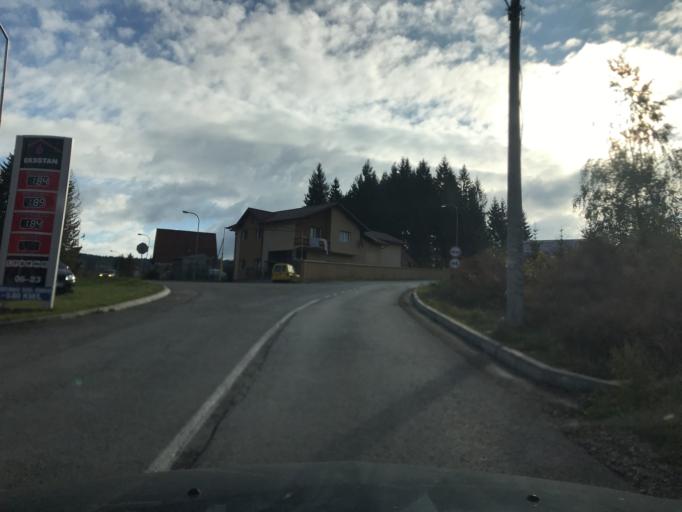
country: BA
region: Republika Srpska
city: Skender Vakuf
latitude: 44.4947
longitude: 17.3730
